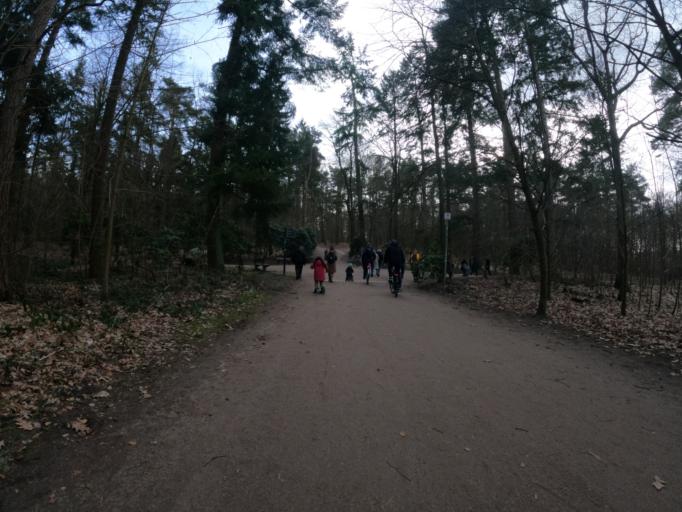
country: DE
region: Hamburg
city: Eidelstedt
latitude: 53.5820
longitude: 9.8921
